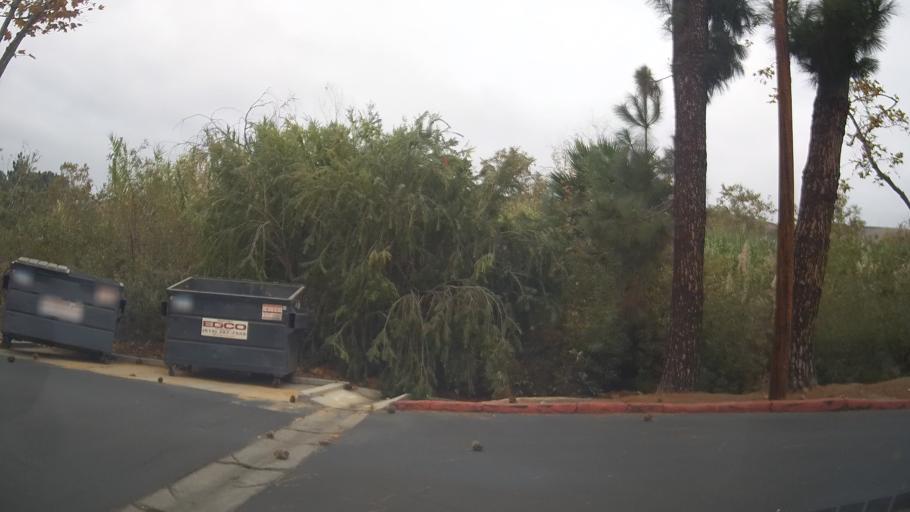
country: US
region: California
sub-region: San Diego County
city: La Jolla
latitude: 32.8942
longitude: -117.2188
